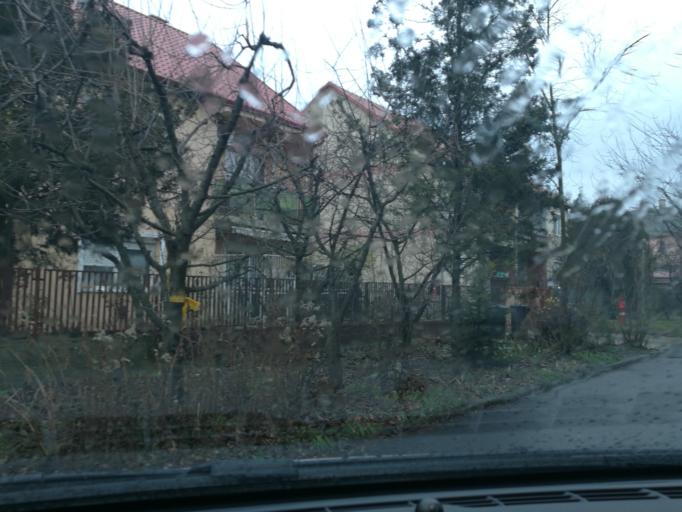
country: HU
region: Szabolcs-Szatmar-Bereg
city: Nyiregyhaza
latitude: 47.9681
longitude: 21.7026
